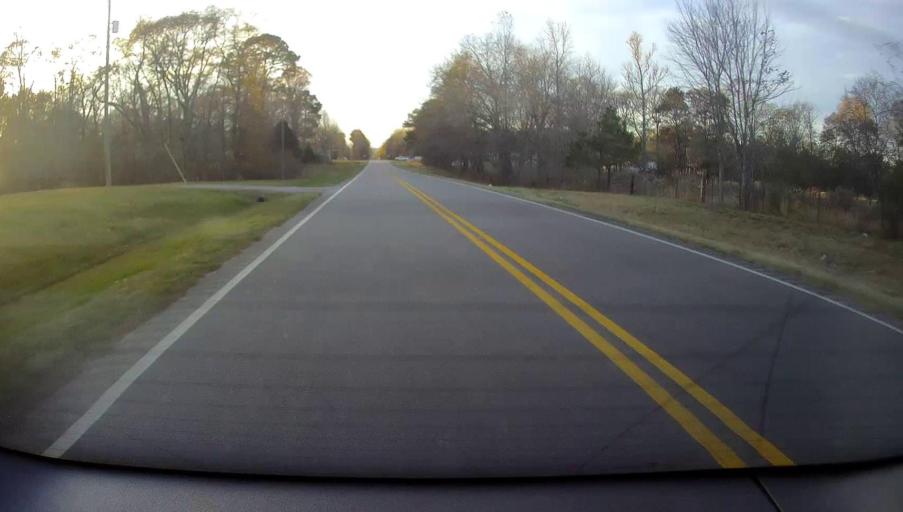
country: US
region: Alabama
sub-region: Etowah County
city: Attalla
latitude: 34.0535
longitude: -86.1974
